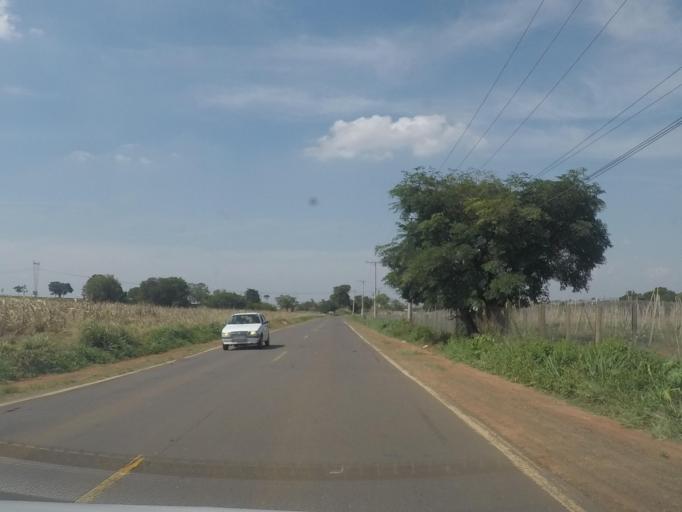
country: BR
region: Sao Paulo
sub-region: Sumare
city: Sumare
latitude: -22.8691
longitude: -47.2972
